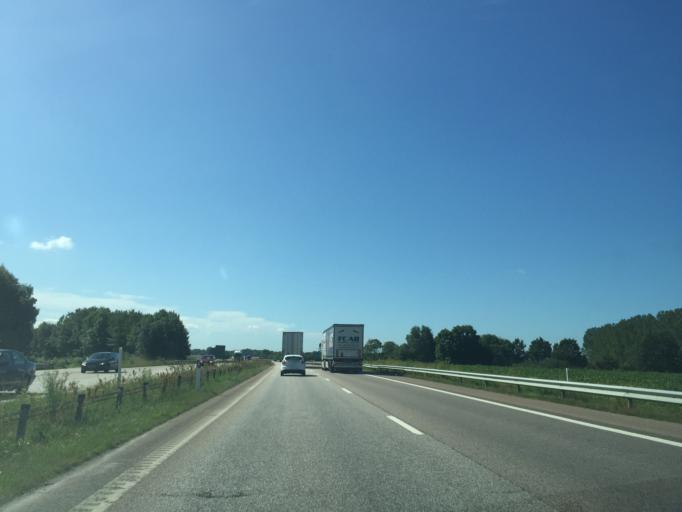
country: SE
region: Skane
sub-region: Angelholms Kommun
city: Strovelstorp
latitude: 56.1779
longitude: 12.8480
